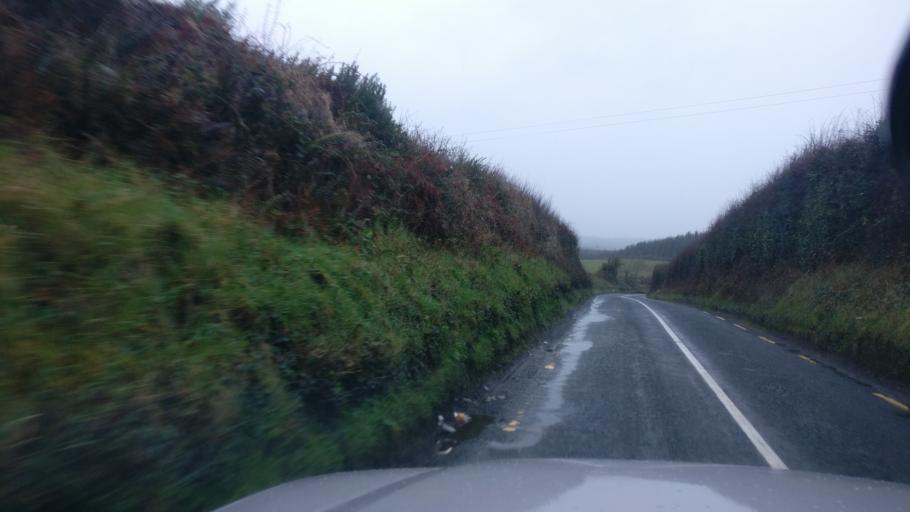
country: IE
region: Connaught
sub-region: County Galway
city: Loughrea
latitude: 53.1188
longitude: -8.4453
